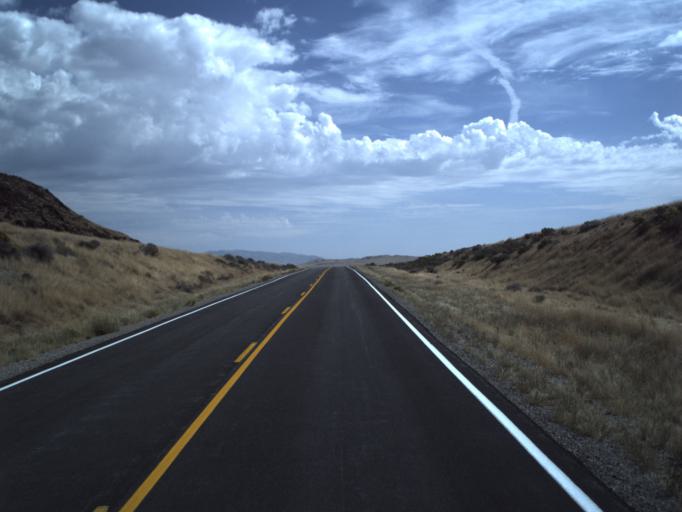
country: US
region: Utah
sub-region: Tooele County
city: Wendover
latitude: 41.3757
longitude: -114.0121
